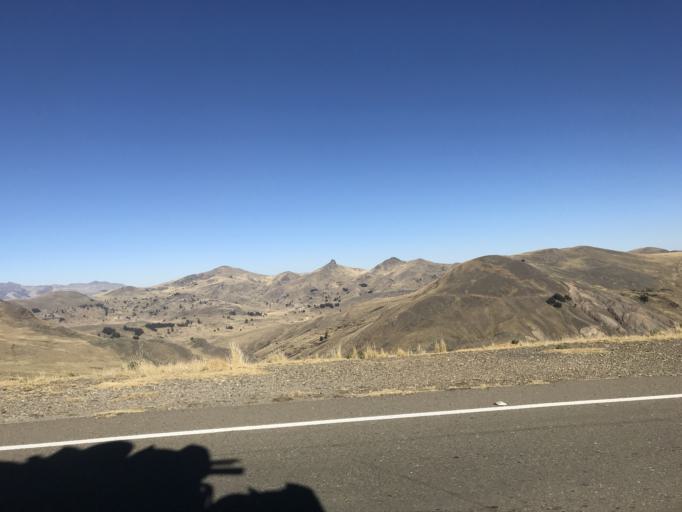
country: PE
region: Puno
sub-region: Yunguyo
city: Yunguyo
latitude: -16.1612
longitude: -68.9905
